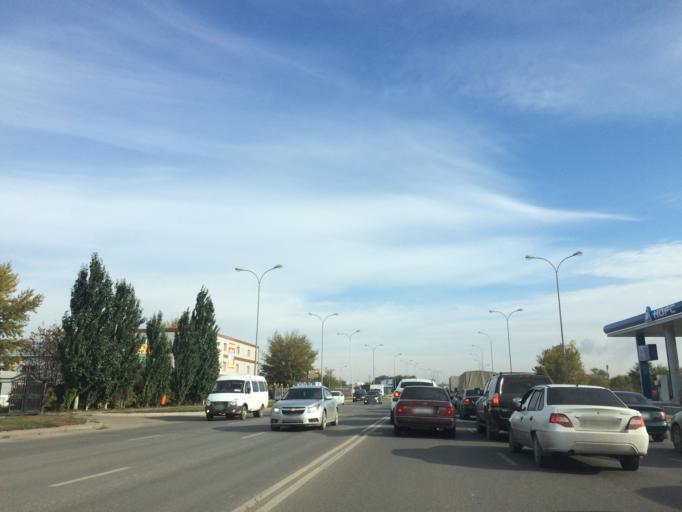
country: KZ
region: Astana Qalasy
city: Astana
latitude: 51.1668
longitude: 71.4766
